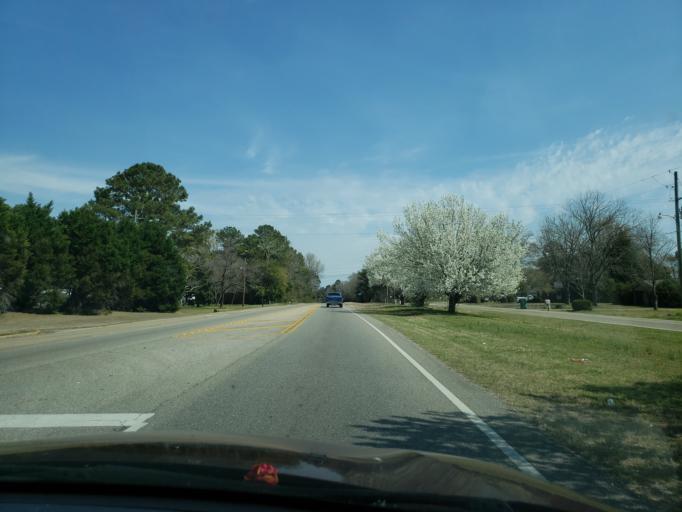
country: US
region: Alabama
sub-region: Elmore County
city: Elmore
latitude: 32.5290
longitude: -86.3489
